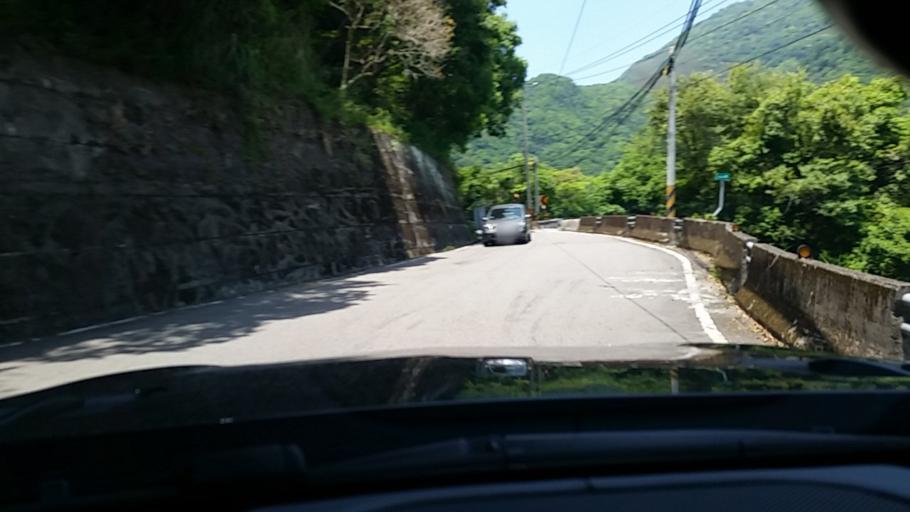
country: TW
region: Taiwan
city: Daxi
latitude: 24.6983
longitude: 121.3751
